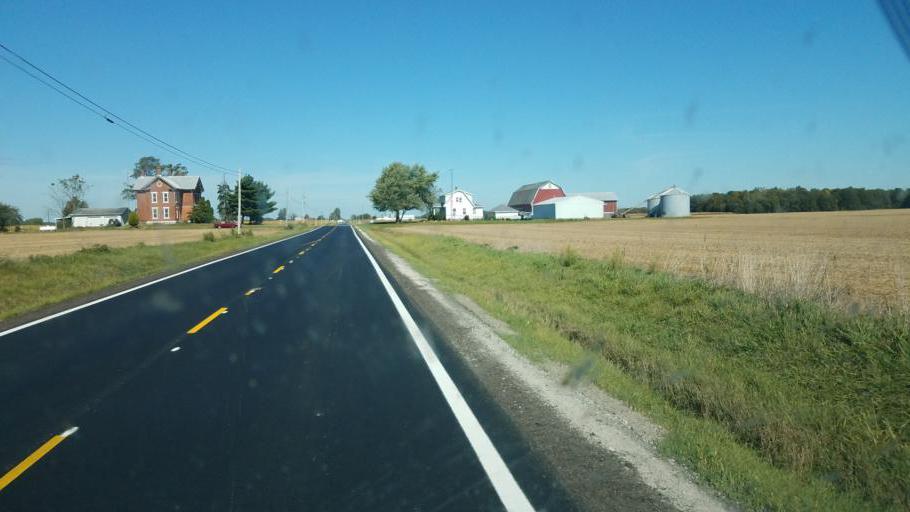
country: US
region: Ohio
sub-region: Crawford County
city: Bucyrus
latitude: 40.9405
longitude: -83.0164
